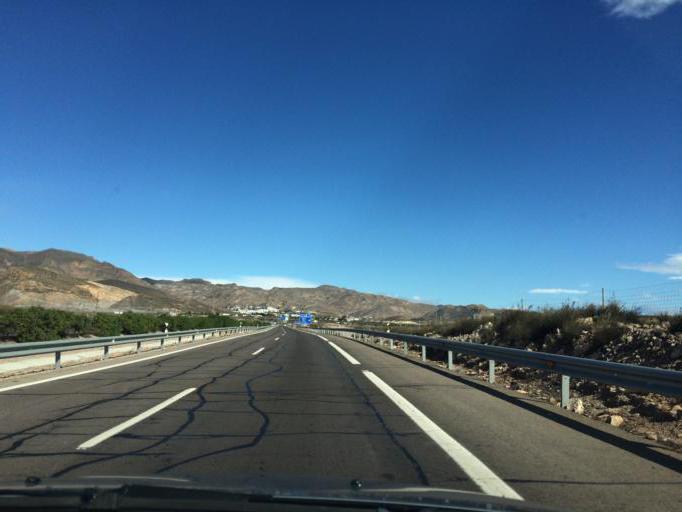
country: ES
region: Andalusia
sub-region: Provincia de Almeria
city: Nijar
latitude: 36.9268
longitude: -2.2095
